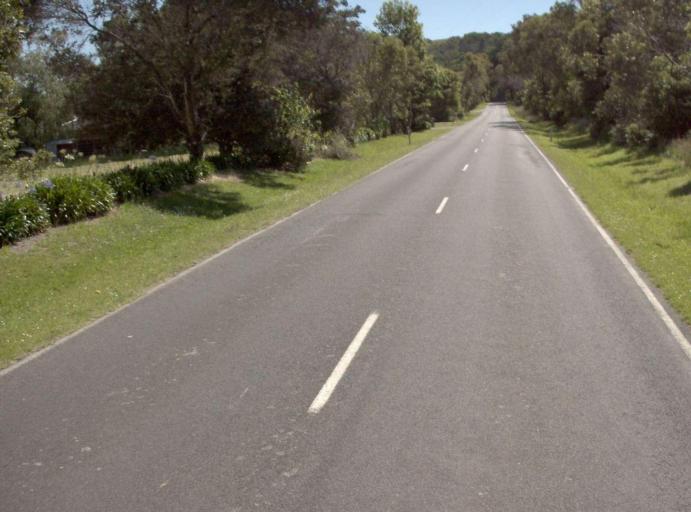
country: AU
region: Victoria
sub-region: Latrobe
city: Morwell
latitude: -38.6660
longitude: 146.1782
